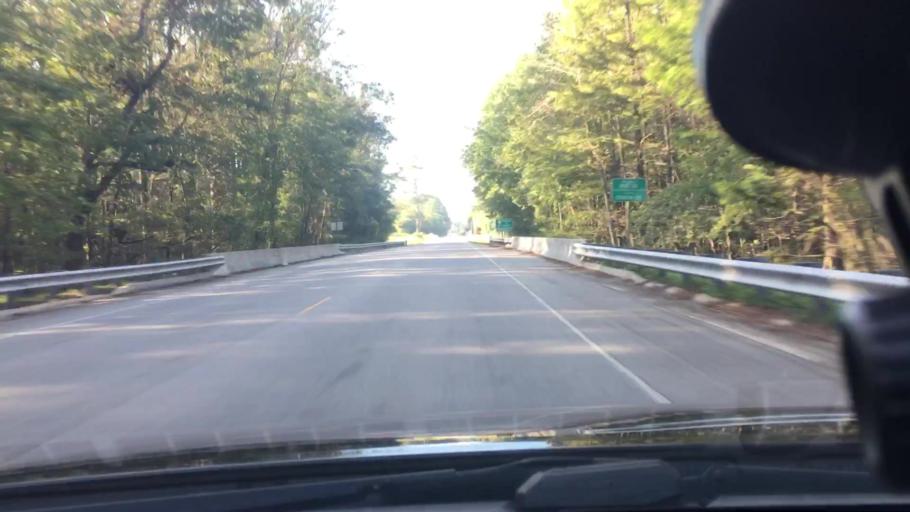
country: US
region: North Carolina
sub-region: Craven County
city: Vanceboro
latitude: 35.3915
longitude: -77.2312
